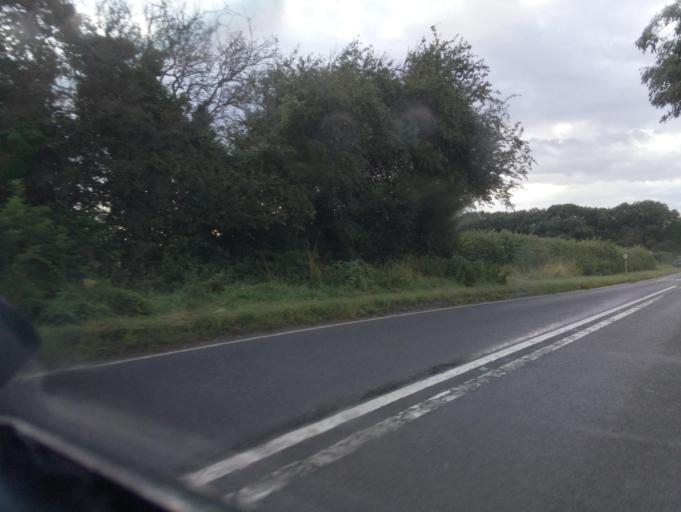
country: GB
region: England
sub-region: Oxfordshire
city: Woodstock
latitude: 51.8512
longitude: -1.3153
